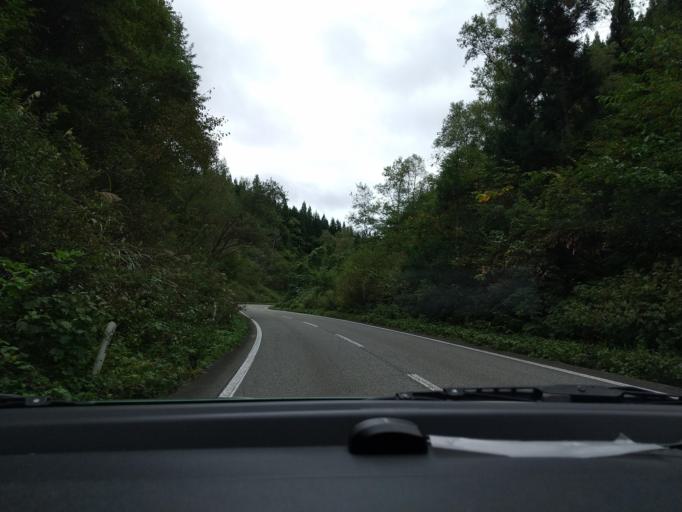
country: JP
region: Akita
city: Kakunodatemachi
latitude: 39.5521
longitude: 140.6334
